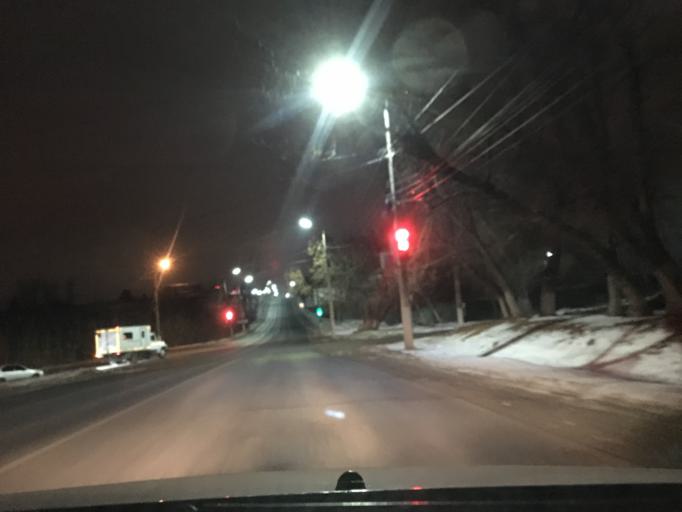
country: RU
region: Tula
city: Mendeleyevskiy
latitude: 54.1343
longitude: 37.5793
